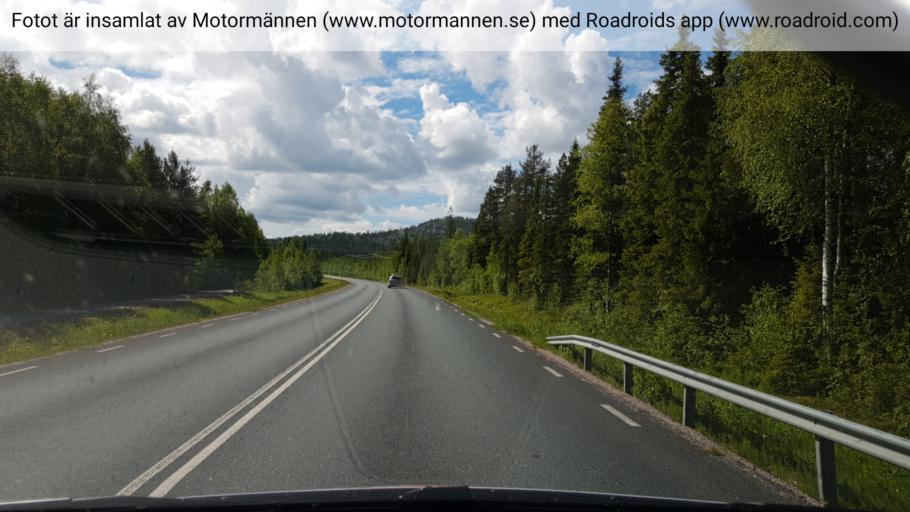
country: FI
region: Lapland
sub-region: Torniolaakso
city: Ylitornio
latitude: 66.3255
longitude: 23.6246
